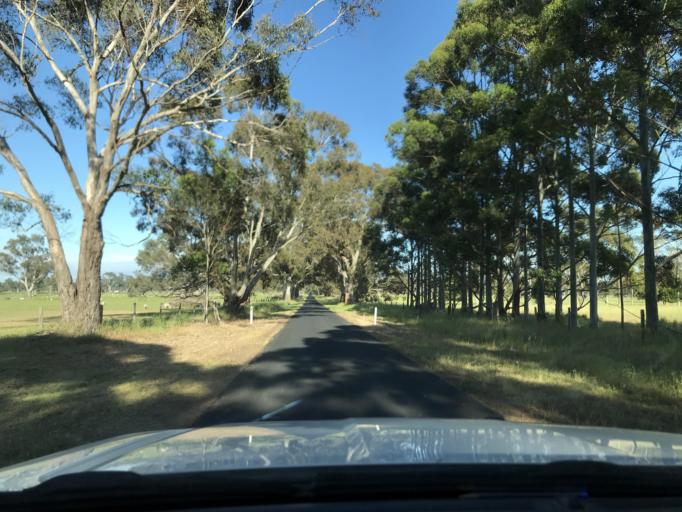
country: AU
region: South Australia
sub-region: Wattle Range
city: Penola
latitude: -37.2024
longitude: 140.9985
